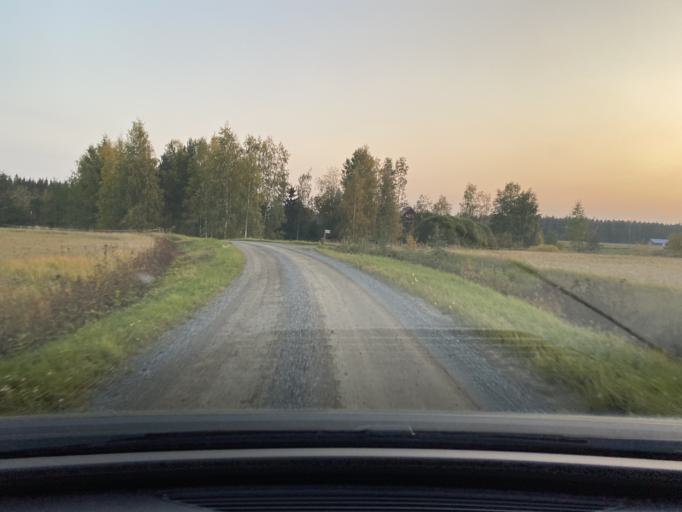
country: FI
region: Pirkanmaa
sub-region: Lounais-Pirkanmaa
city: Punkalaidun
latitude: 61.1143
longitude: 23.2405
